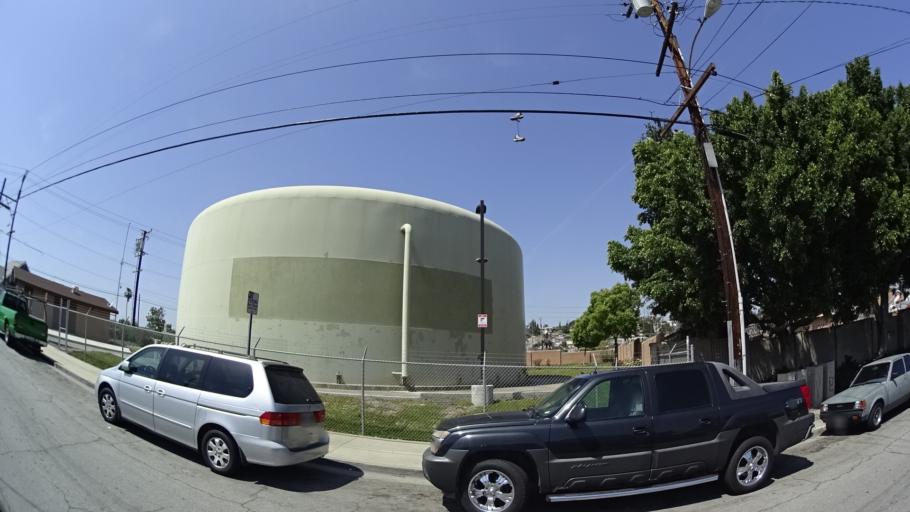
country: US
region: California
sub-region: Los Angeles County
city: Belvedere
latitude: 34.0443
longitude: -118.1865
